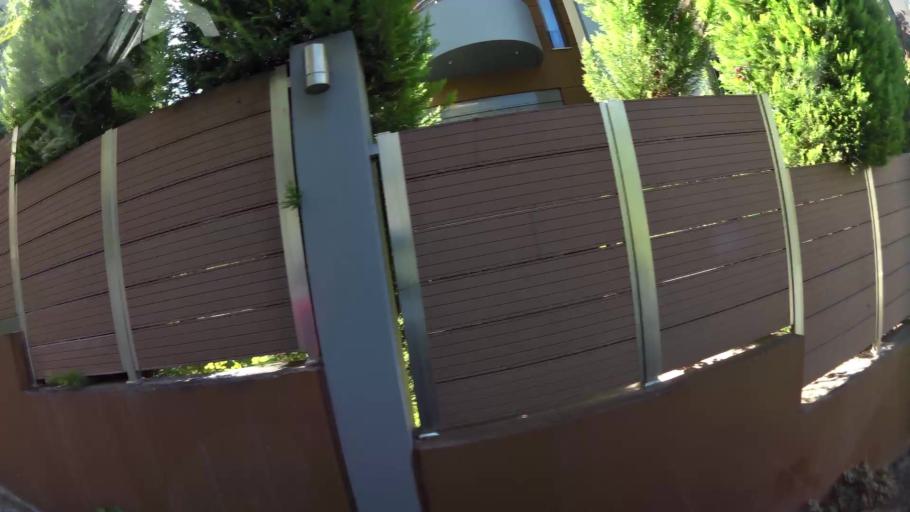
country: GR
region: Attica
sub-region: Nomarchia Athinas
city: Metamorfosi
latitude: 38.0634
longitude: 23.7729
